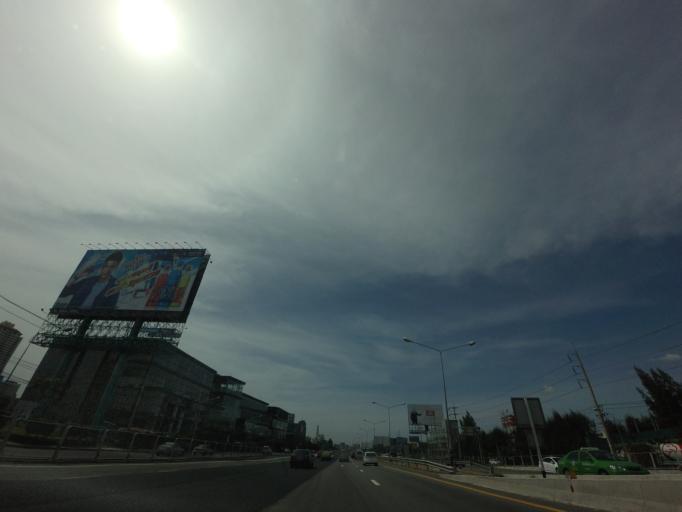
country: TH
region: Bangkok
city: Suan Luang
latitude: 13.7394
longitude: 100.6513
